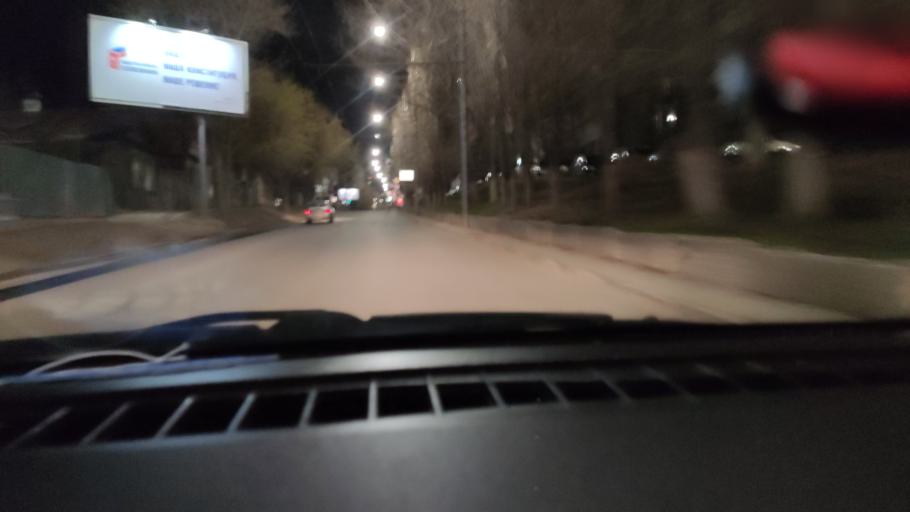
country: RU
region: Saratov
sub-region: Saratovskiy Rayon
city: Saratov
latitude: 51.5318
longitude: 46.0611
